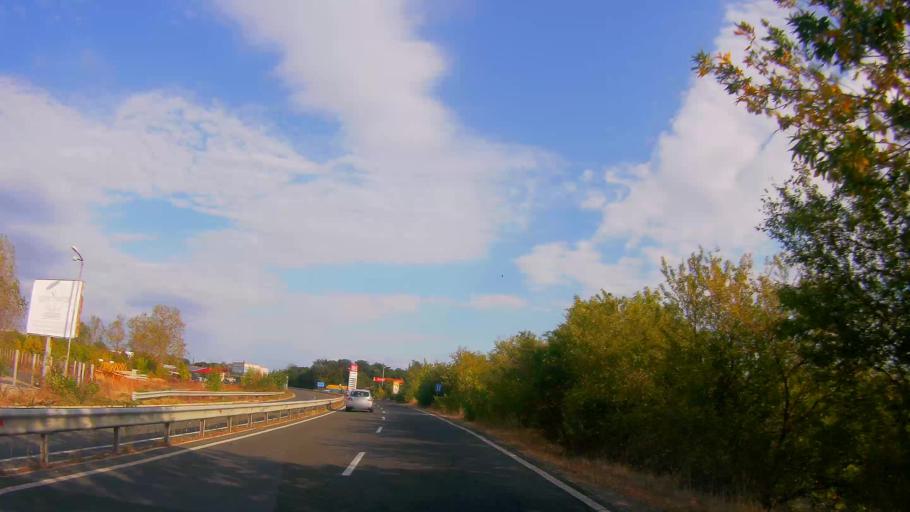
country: BG
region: Burgas
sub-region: Obshtina Sozopol
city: Chernomorets
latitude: 42.4373
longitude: 27.6370
